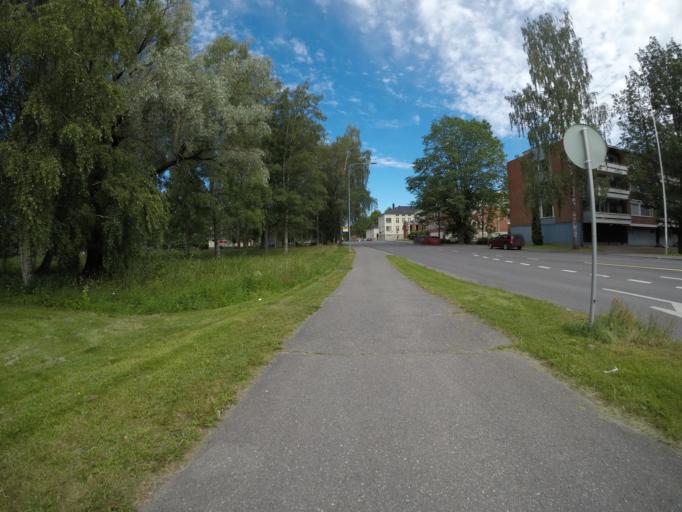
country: FI
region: Haeme
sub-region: Haemeenlinna
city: Haemeenlinna
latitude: 61.0000
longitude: 24.4590
